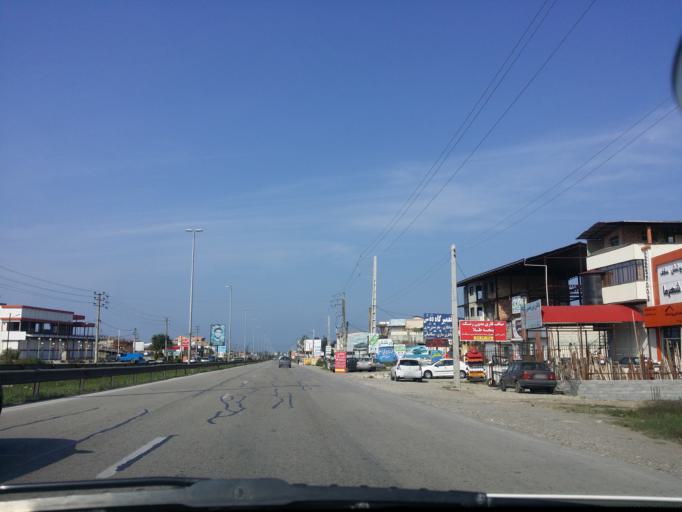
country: IR
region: Mazandaran
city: Chalus
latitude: 36.6615
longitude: 51.3993
